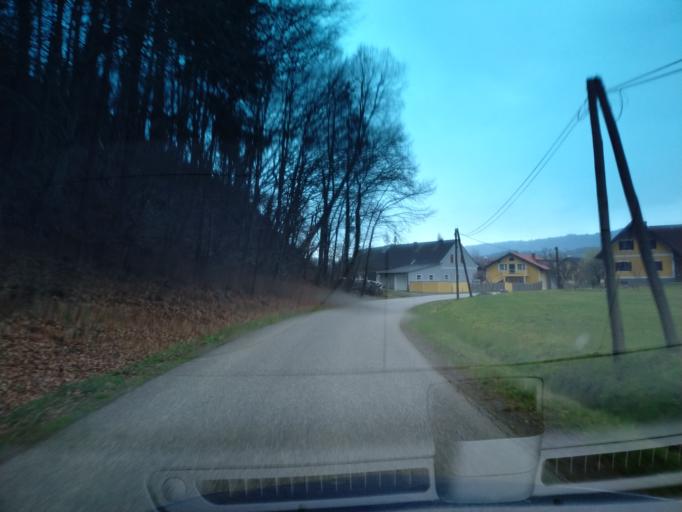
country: AT
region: Styria
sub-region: Politischer Bezirk Leibnitz
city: Oberhaag
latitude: 46.6978
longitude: 15.3658
